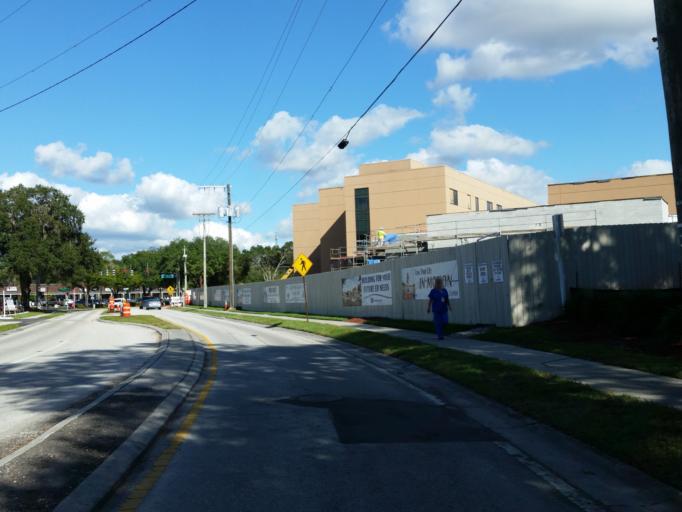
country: US
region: Florida
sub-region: Hillsborough County
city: Brandon
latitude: 27.9332
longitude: -82.2892
